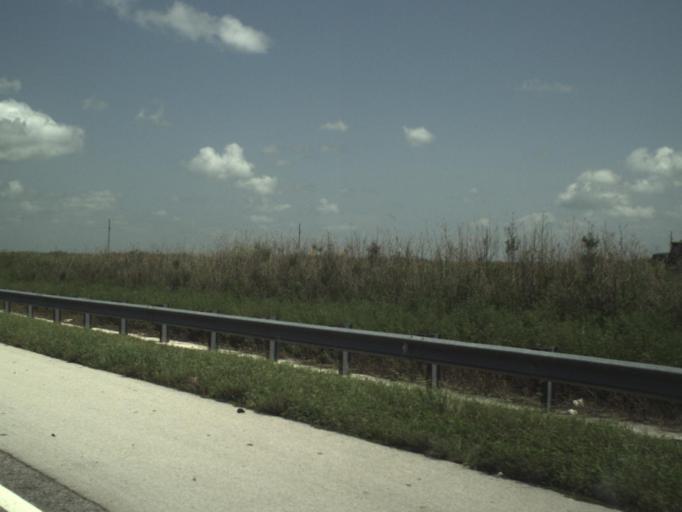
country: US
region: Florida
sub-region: Palm Beach County
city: Belle Glade Camp
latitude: 26.3745
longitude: -80.5683
